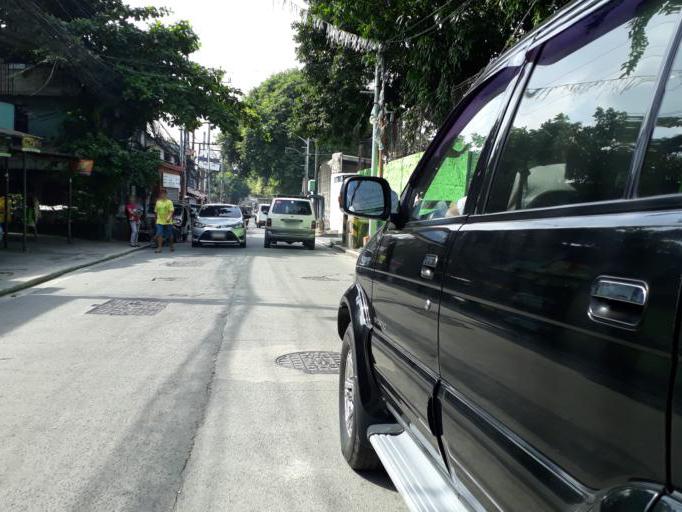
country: PH
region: Calabarzon
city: Bagong Pagasa
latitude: 14.6715
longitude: 121.0057
